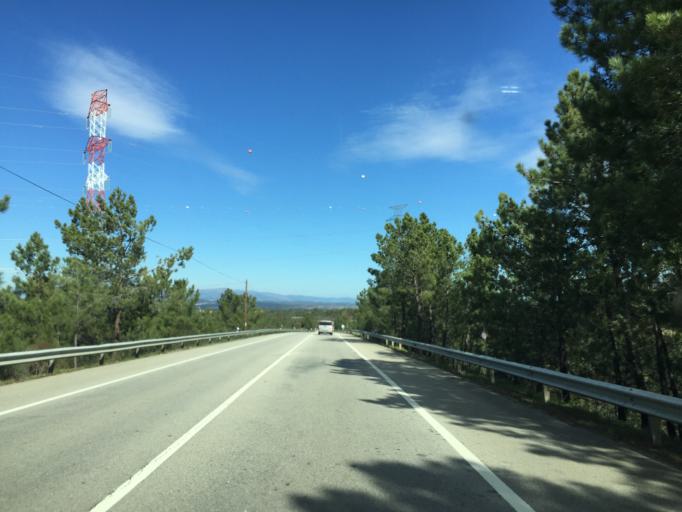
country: PT
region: Castelo Branco
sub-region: Castelo Branco
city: Castelo Branco
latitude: 39.7723
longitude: -7.5866
